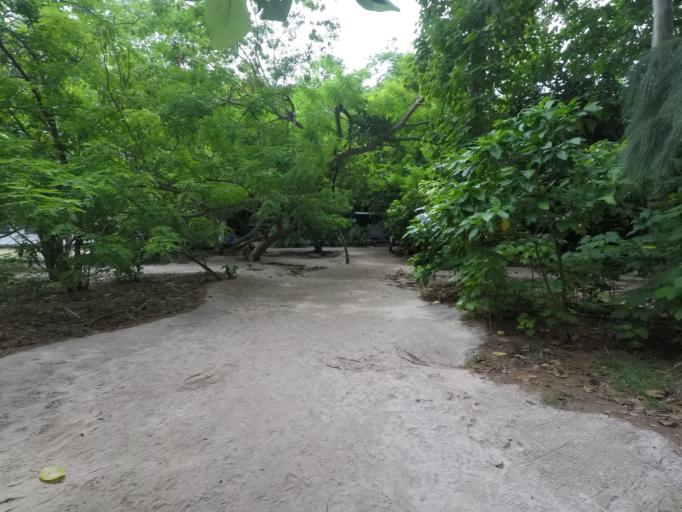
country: TH
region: Phangnga
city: Ban Ao Nang
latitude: 7.8180
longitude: 98.7972
